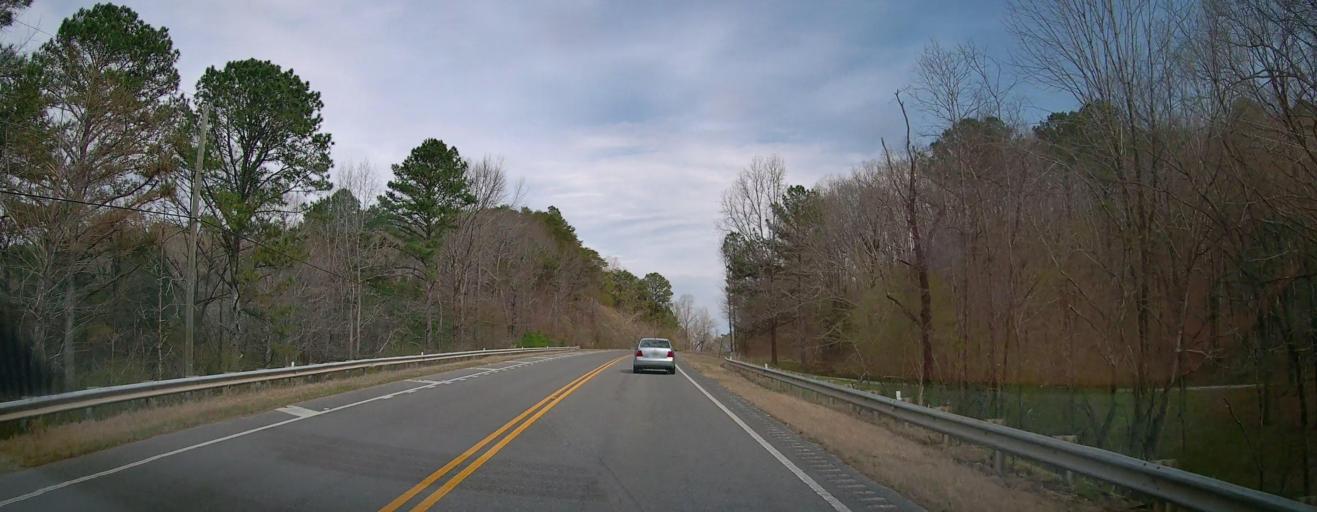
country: US
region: Alabama
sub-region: Walker County
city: Carbon Hill
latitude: 33.9175
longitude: -87.5711
